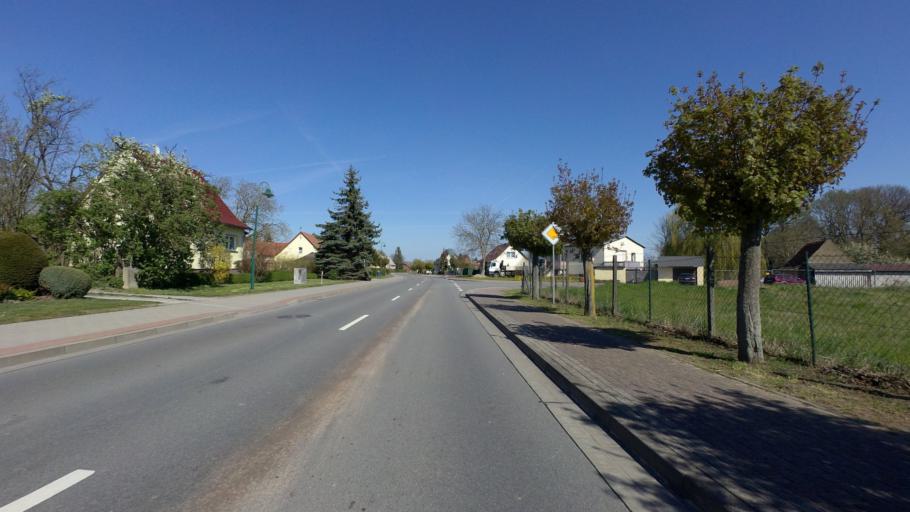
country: DE
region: Saxony-Anhalt
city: Kalbe
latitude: 52.6473
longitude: 11.3391
